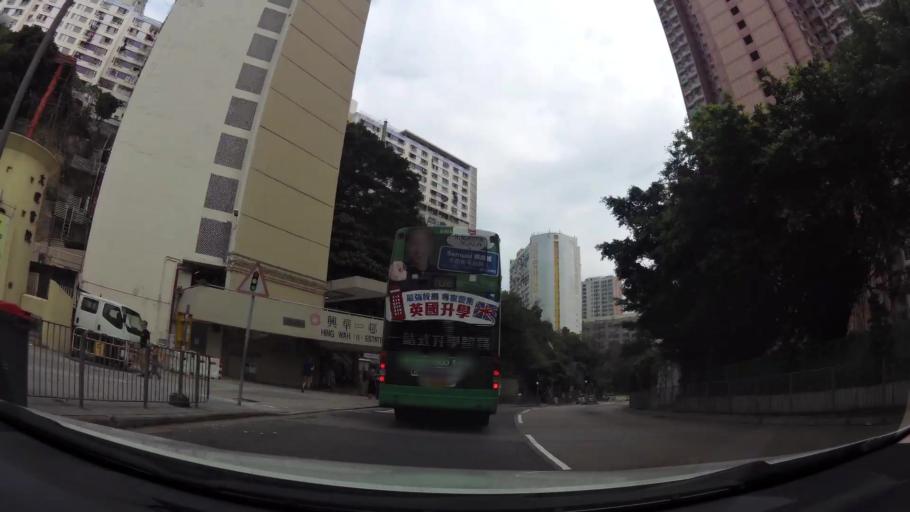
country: HK
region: Wanchai
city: Wan Chai
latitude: 22.2624
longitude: 114.2343
